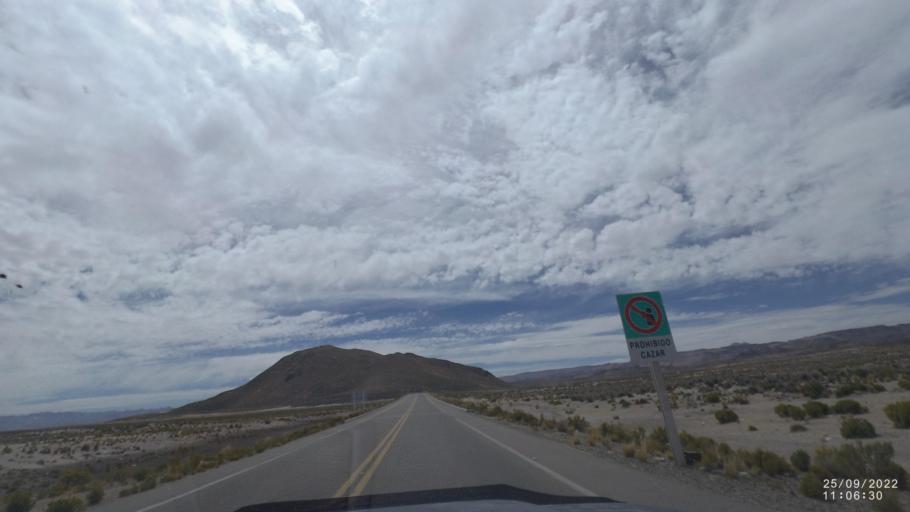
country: BO
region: Oruro
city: Challapata
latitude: -19.3560
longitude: -66.8624
